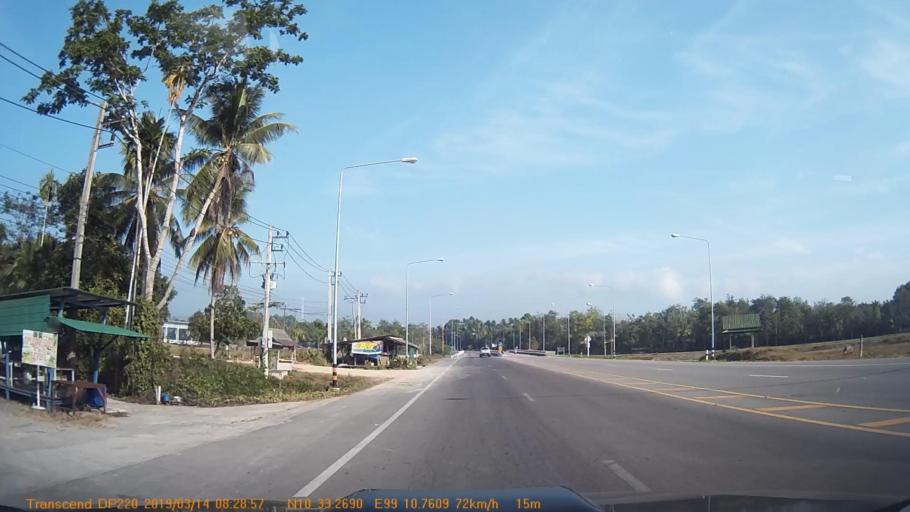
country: TH
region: Chumphon
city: Chumphon
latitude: 10.5544
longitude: 99.1793
